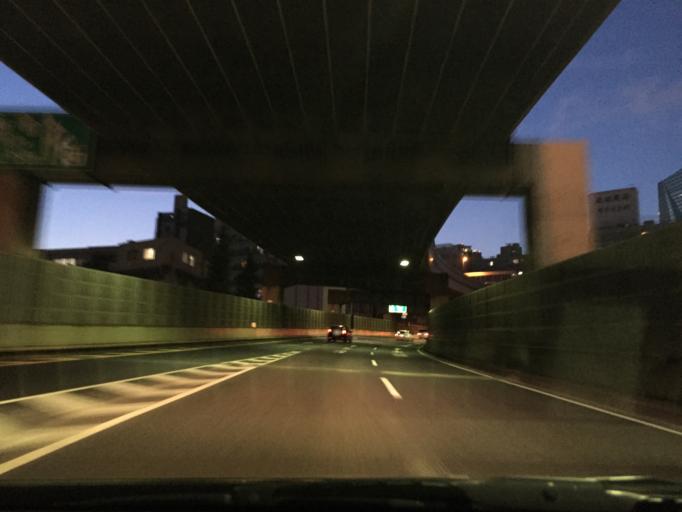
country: JP
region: Tokyo
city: Tokyo
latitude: 35.6572
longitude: 139.7367
